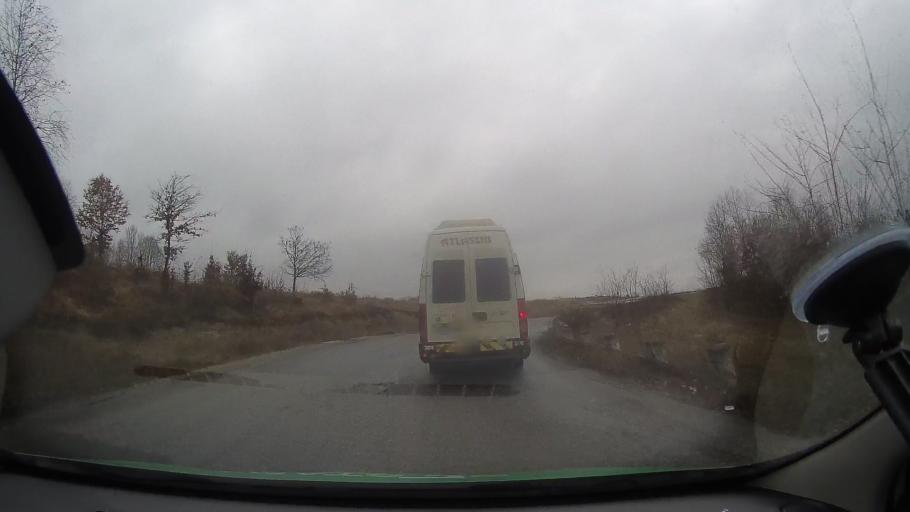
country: RO
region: Arad
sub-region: Comuna Halmagiu
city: Halmagiu
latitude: 46.2862
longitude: 22.5540
